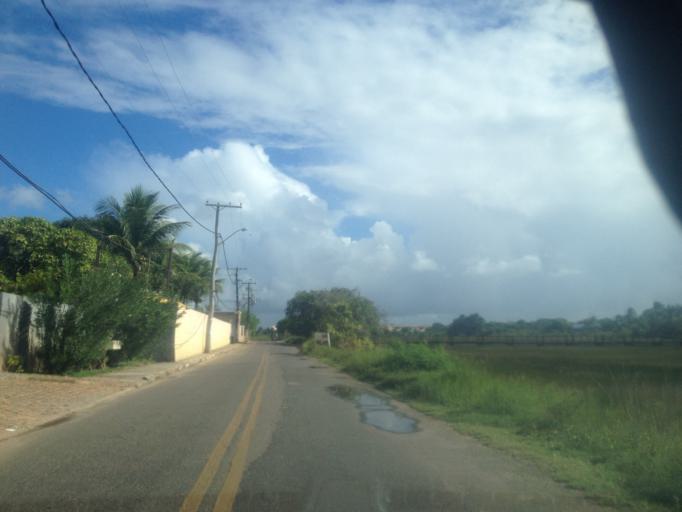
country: BR
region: Bahia
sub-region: Mata De Sao Joao
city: Mata de Sao Joao
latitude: -12.6195
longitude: -38.0463
